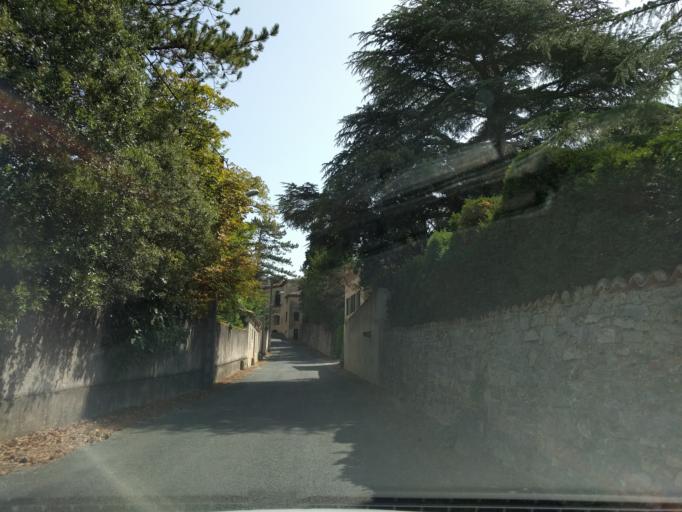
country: FR
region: Midi-Pyrenees
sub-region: Departement du Tarn
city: Castres
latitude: 43.5995
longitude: 2.2482
